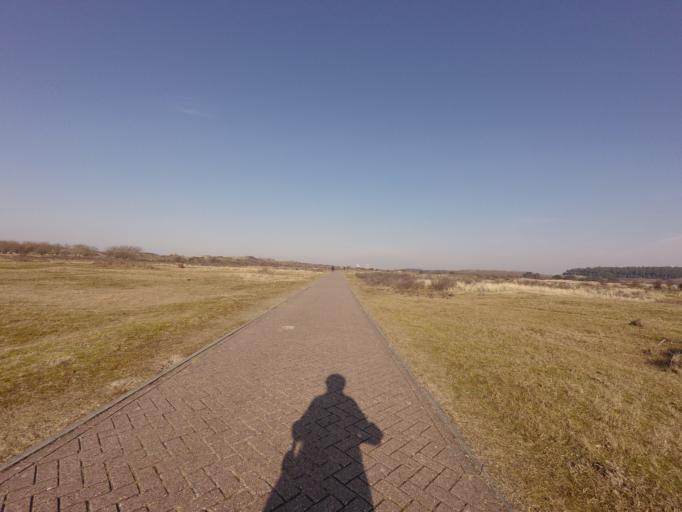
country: NL
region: North Holland
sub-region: Gemeente Bloemendaal
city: Bloemendaal
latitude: 52.4207
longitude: 4.5724
